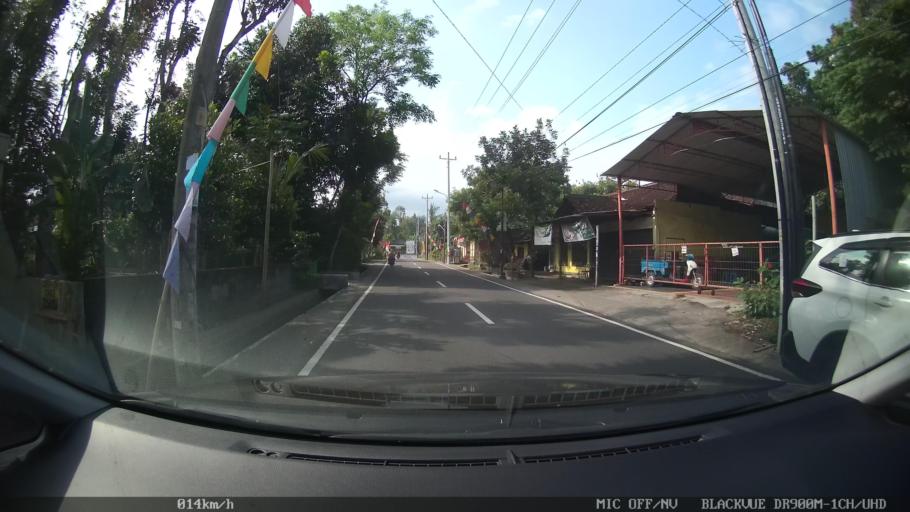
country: ID
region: Daerah Istimewa Yogyakarta
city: Depok
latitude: -7.7294
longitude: 110.4227
